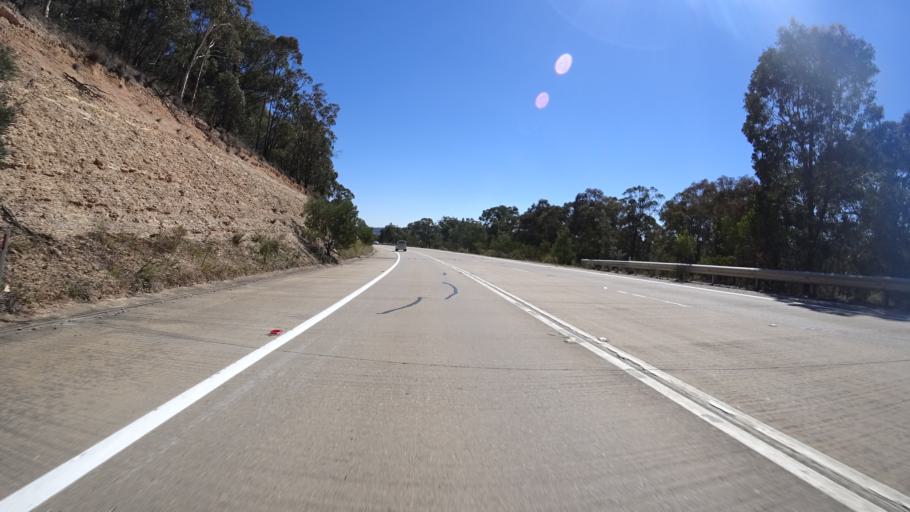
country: AU
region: New South Wales
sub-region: Lithgow
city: Portland
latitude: -33.3311
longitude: 150.0369
